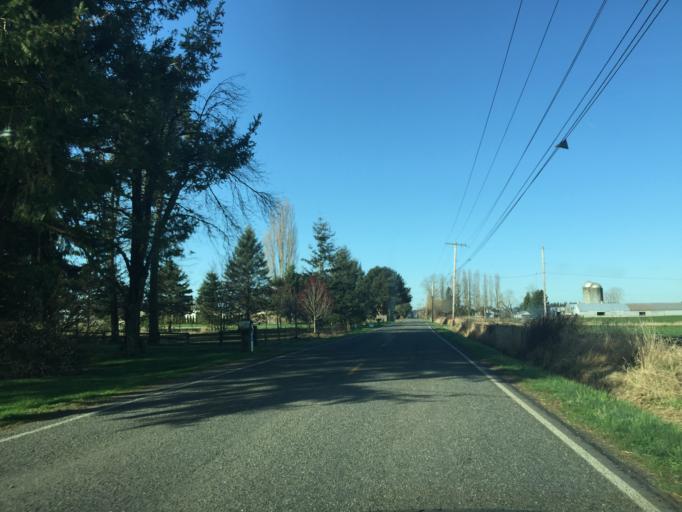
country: US
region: Washington
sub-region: Whatcom County
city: Marietta-Alderwood
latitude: 48.8552
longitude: -122.5061
